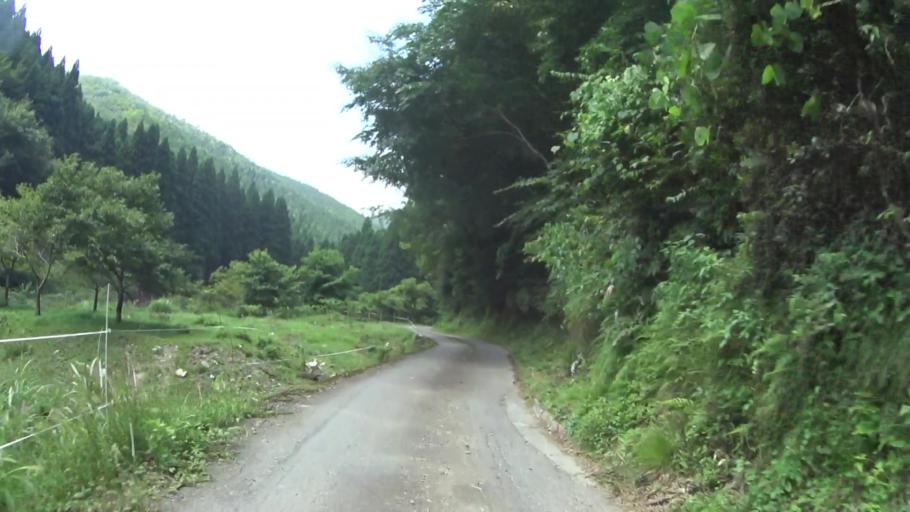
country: JP
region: Kyoto
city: Ayabe
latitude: 35.3009
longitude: 135.4024
